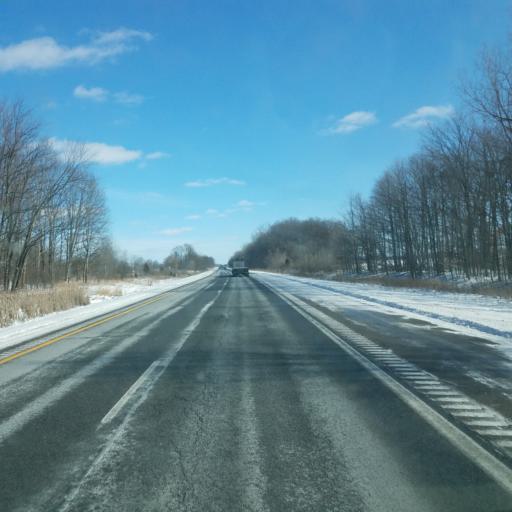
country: US
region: Michigan
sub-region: Ingham County
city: Williamston
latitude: 42.6656
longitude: -84.3300
